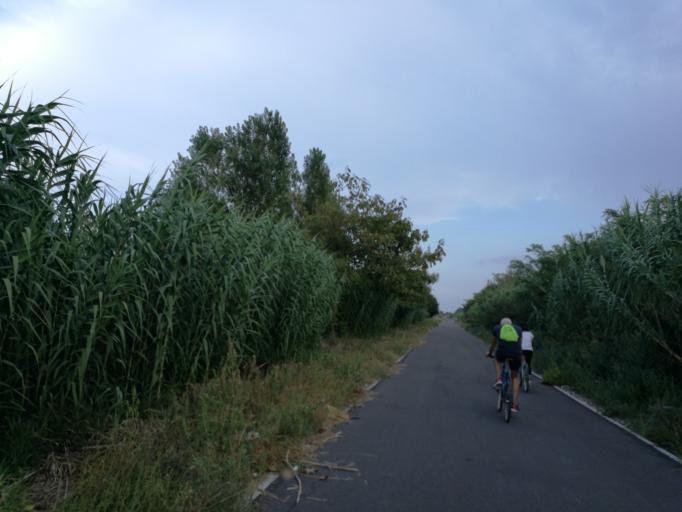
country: IT
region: Abruzzo
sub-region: Provincia di Chieti
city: Fossacesia
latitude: 42.2443
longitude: 14.5201
